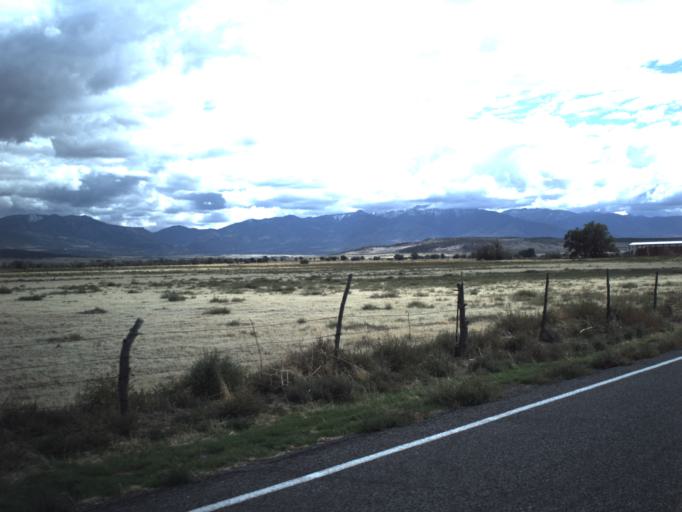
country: US
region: Utah
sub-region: Millard County
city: Fillmore
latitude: 39.0633
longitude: -112.4098
